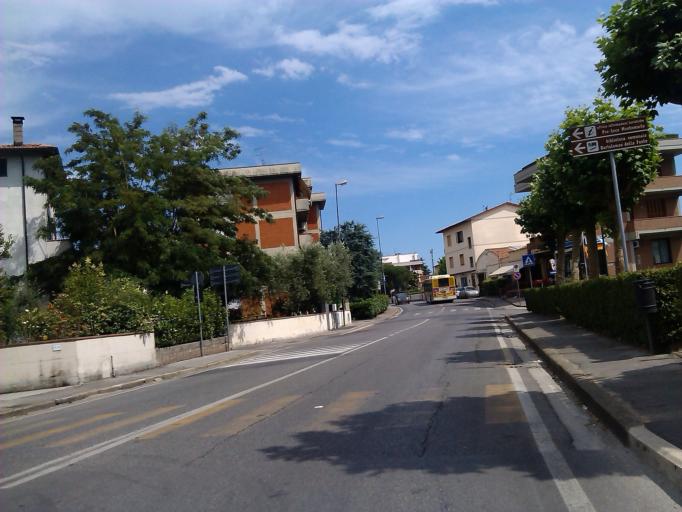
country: IT
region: Tuscany
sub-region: Provincia di Prato
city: Montemurlo
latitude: 43.9293
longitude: 11.0325
